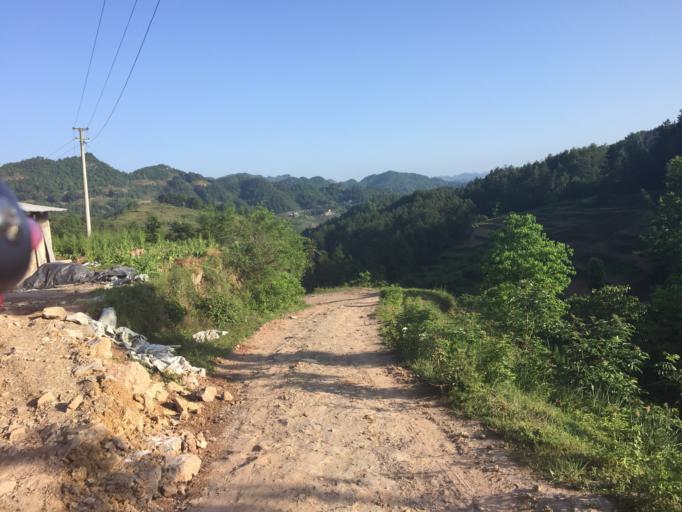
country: CN
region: Guizhou Sheng
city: Xujiaba
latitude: 27.7189
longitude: 108.0231
